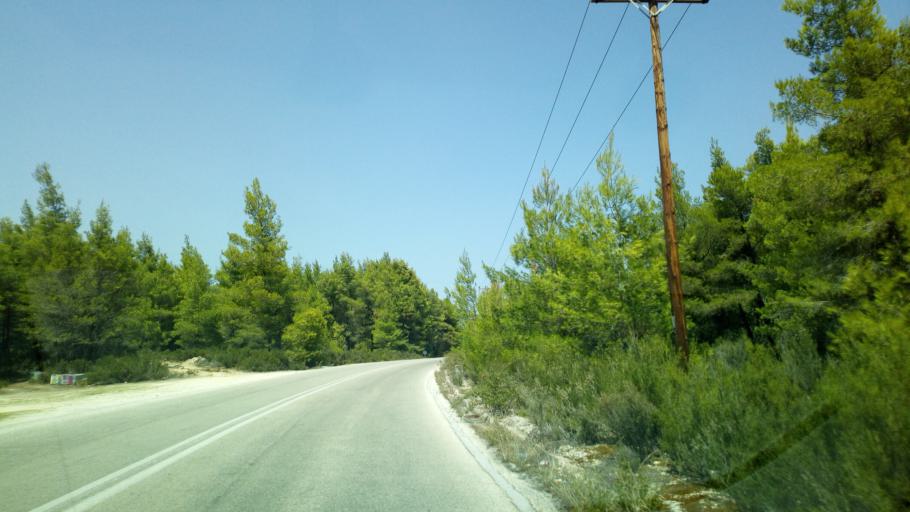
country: GR
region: Central Macedonia
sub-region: Nomos Chalkidikis
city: Sarti
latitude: 40.1363
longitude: 23.9229
